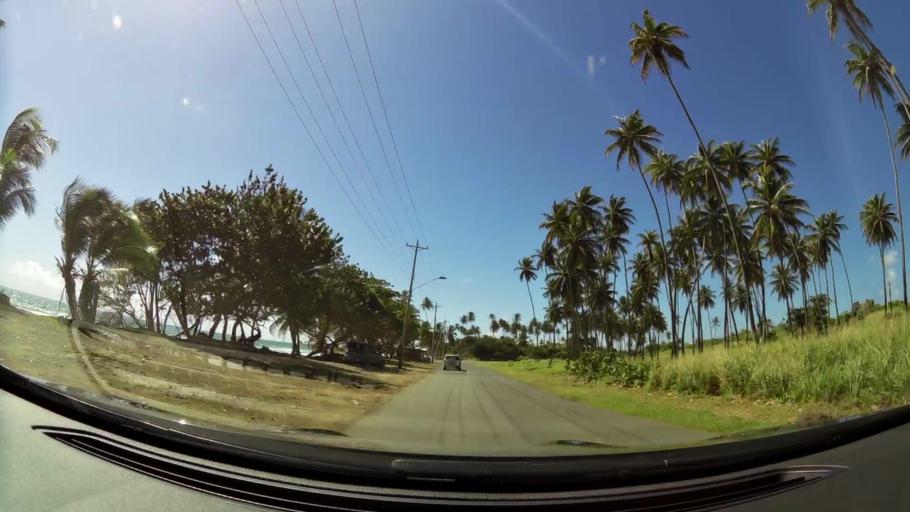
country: TT
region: Tobago
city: Scarborough
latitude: 11.1596
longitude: -60.7694
